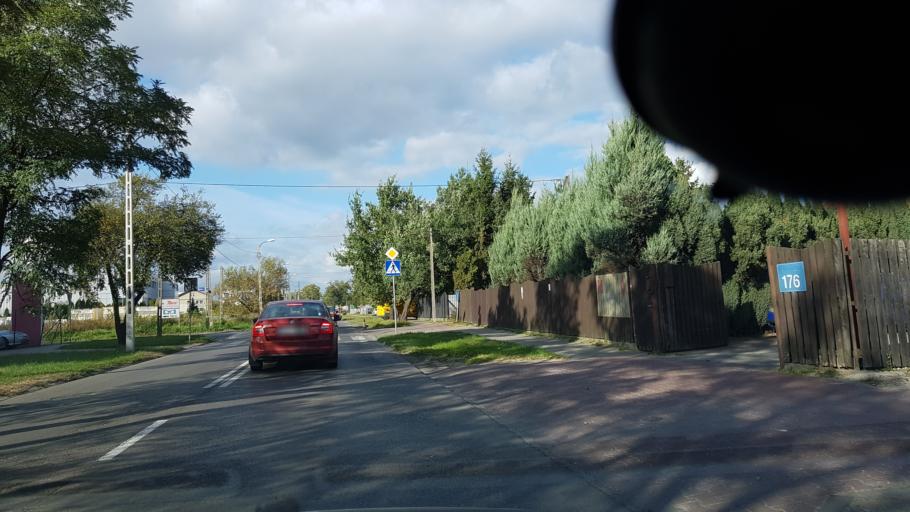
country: PL
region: Masovian Voivodeship
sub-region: Warszawa
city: Targowek
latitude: 52.3090
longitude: 21.0300
